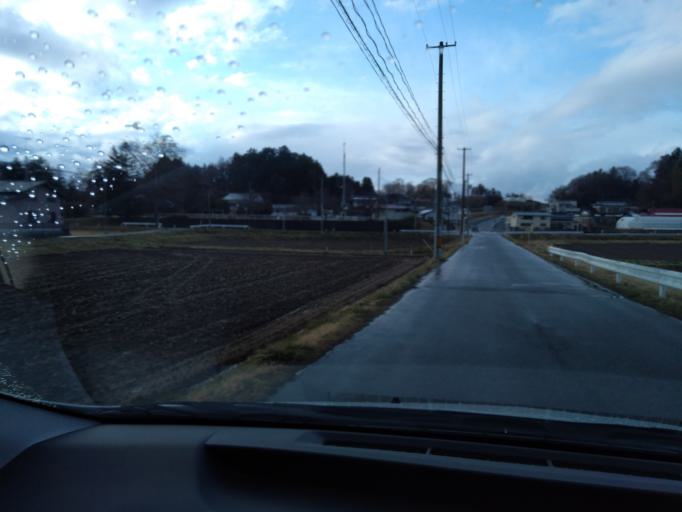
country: JP
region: Iwate
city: Ichinoseki
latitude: 38.7415
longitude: 141.1212
